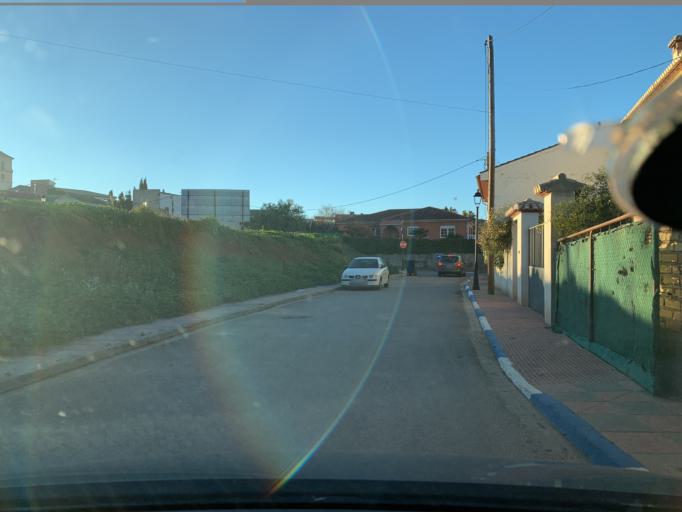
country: ES
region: Andalusia
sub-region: Provincia de Granada
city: Dilar
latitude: 37.0751
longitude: -3.5995
